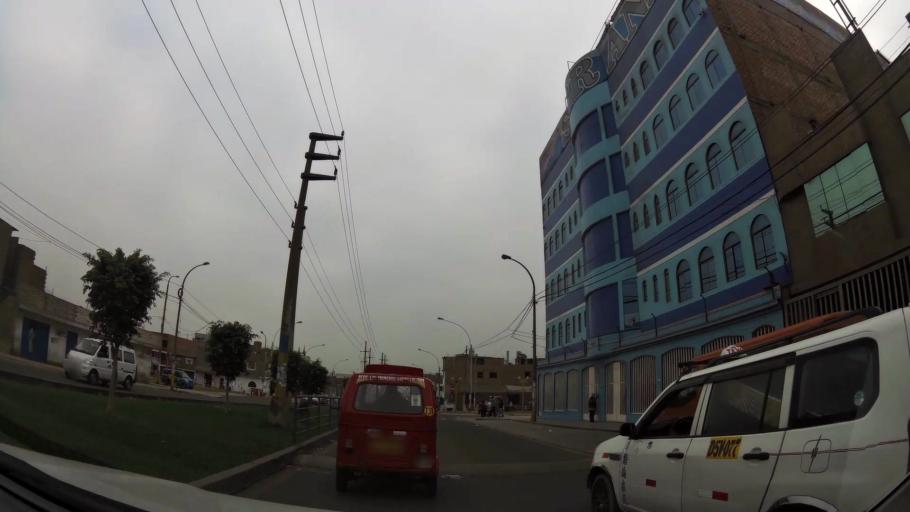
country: PE
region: Lima
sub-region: Lima
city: Independencia
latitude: -11.9662
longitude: -76.9962
